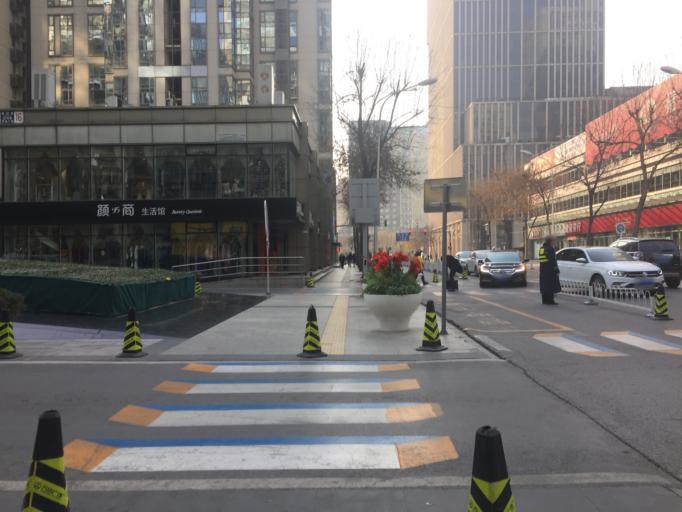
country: CN
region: Beijing
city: Chaowai
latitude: 39.9097
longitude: 116.4655
